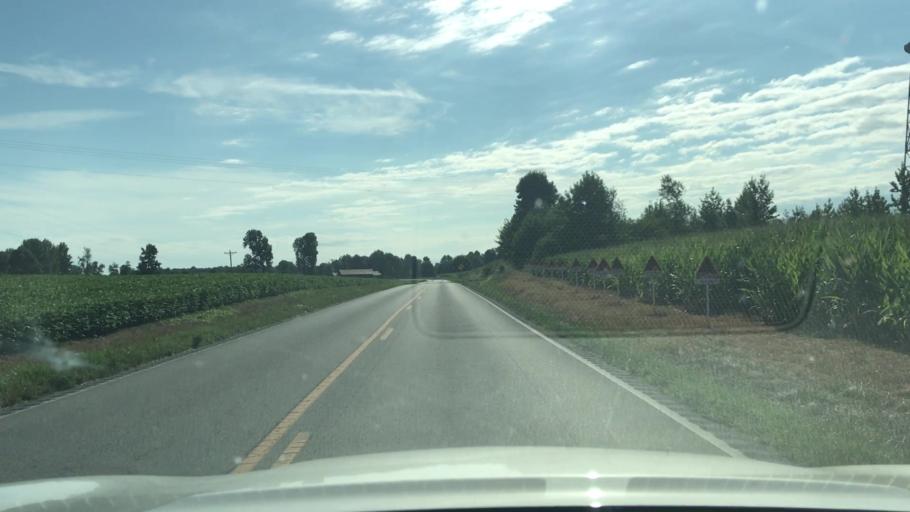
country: US
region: Kentucky
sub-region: Todd County
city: Elkton
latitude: 36.9966
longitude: -87.1414
